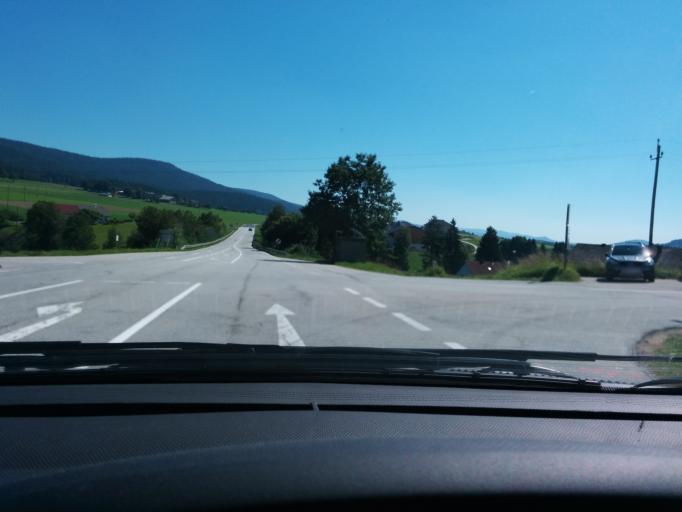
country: AT
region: Upper Austria
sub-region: Politischer Bezirk Rohrbach
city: Ulrichsberg
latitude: 48.6747
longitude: 13.9181
